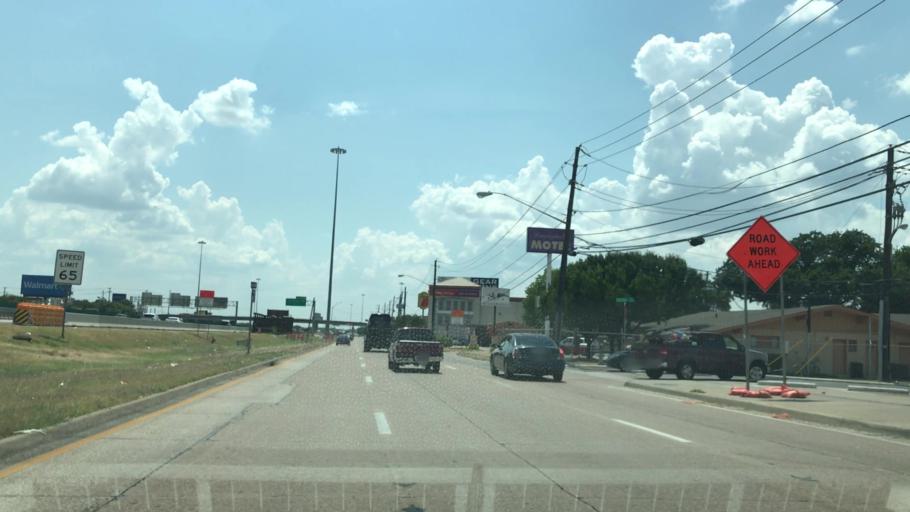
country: US
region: Texas
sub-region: Dallas County
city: Mesquite
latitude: 32.7971
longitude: -96.6879
